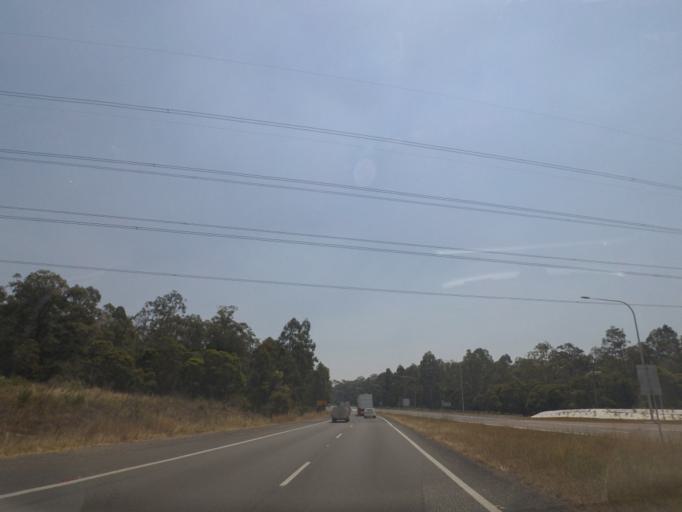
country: AU
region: New South Wales
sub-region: Newcastle
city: Beresfield
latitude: -32.8187
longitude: 151.6348
